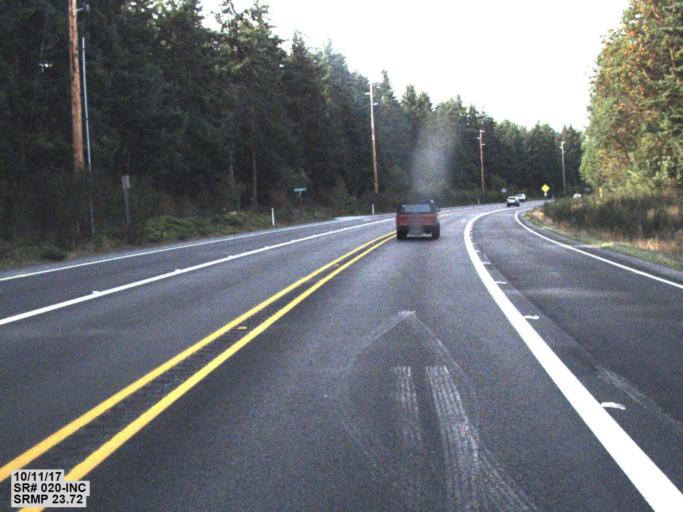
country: US
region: Washington
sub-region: Island County
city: Coupeville
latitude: 48.2112
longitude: -122.7257
